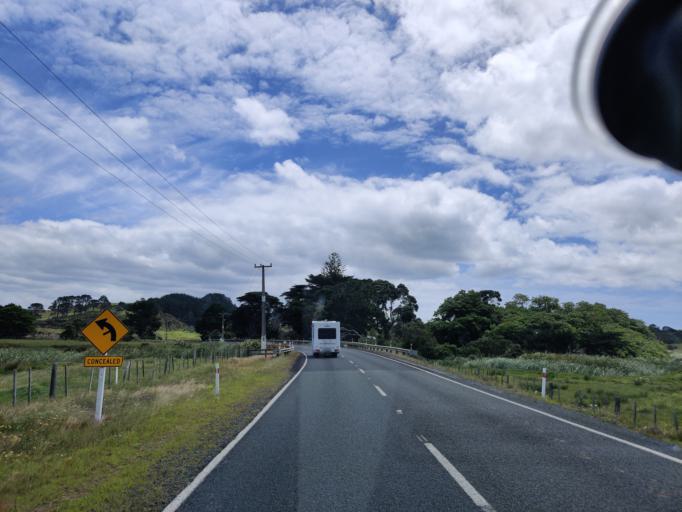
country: NZ
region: Northland
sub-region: Far North District
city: Kaitaia
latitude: -34.7609
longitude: 173.0763
